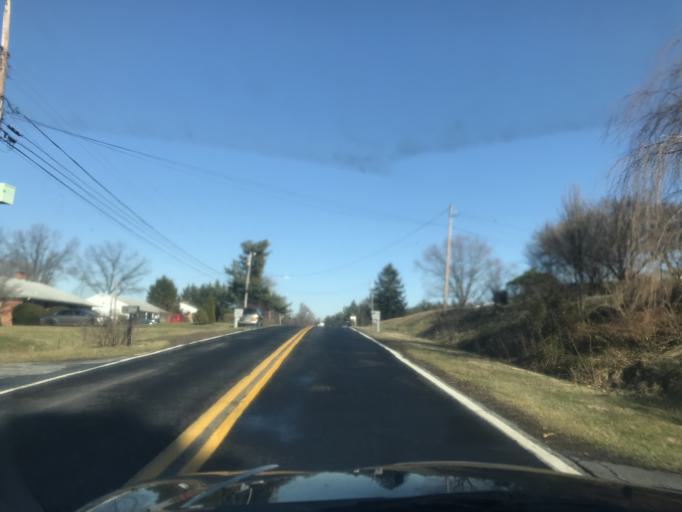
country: US
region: Maryland
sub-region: Montgomery County
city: Damascus
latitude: 39.3022
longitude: -77.1931
